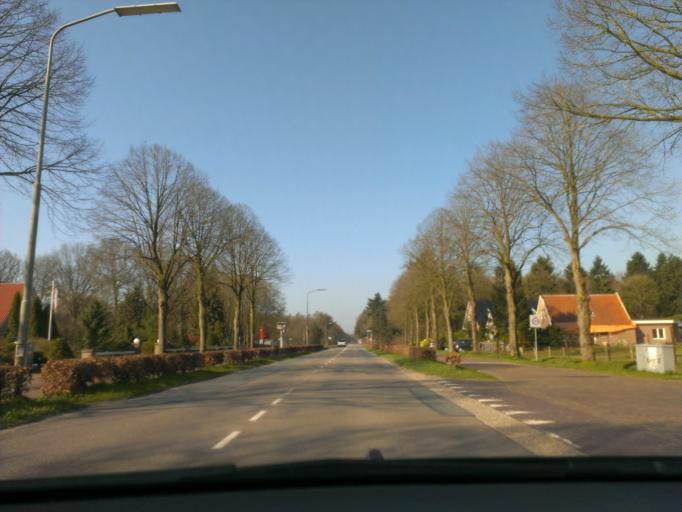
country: NL
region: Drenthe
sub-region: Gemeente Emmen
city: Emmen
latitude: 52.7715
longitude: 6.8769
